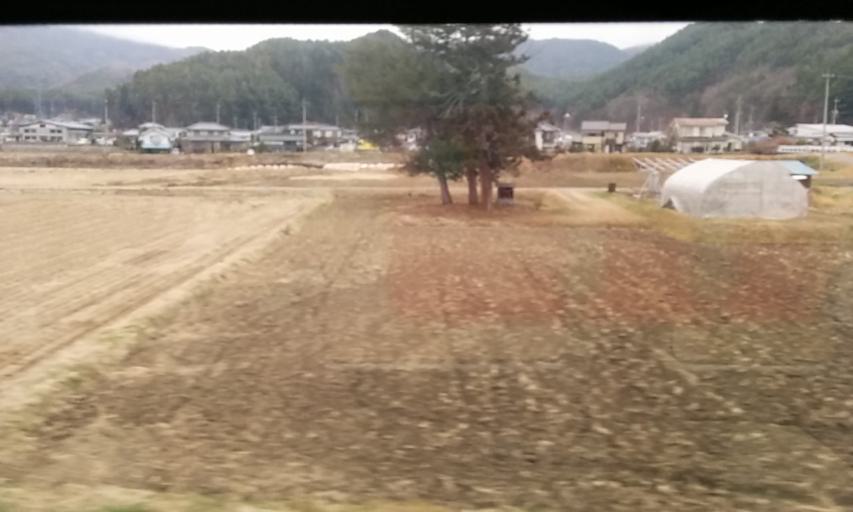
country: JP
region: Nagano
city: Omachi
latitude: 36.4550
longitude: 138.0565
